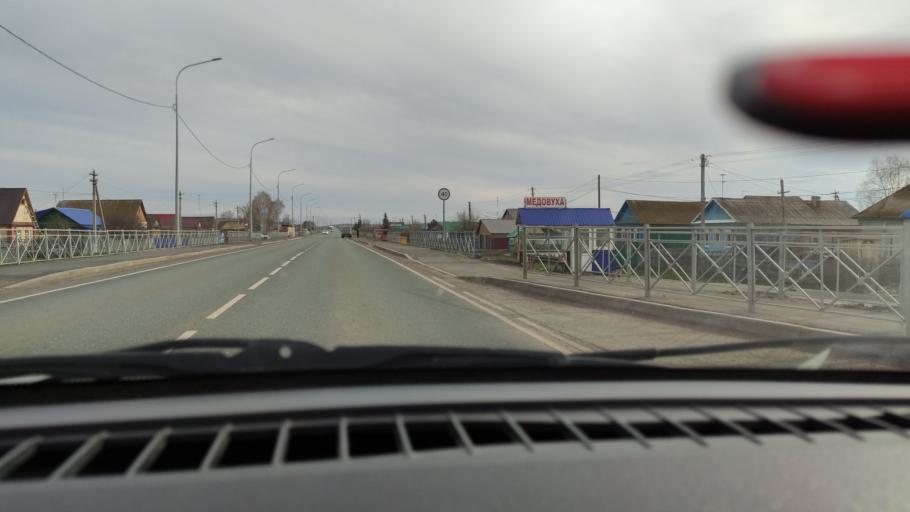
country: RU
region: Bashkortostan
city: Yermolayevo
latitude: 52.5797
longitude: 55.8477
